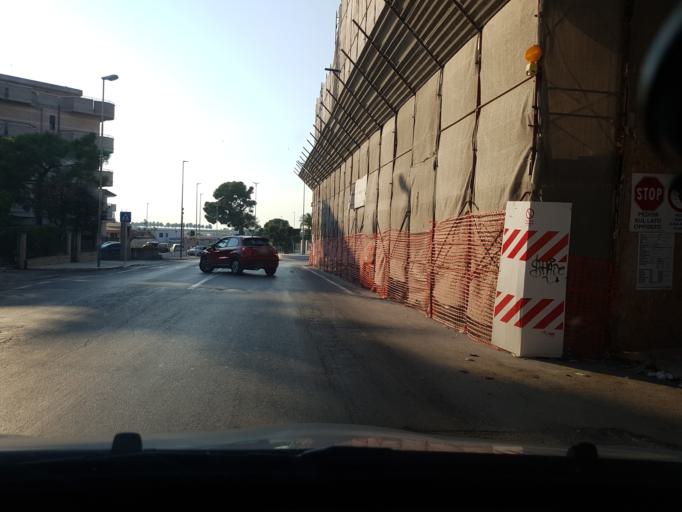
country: IT
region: Apulia
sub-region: Provincia di Foggia
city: Cerignola
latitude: 41.2667
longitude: 15.8861
